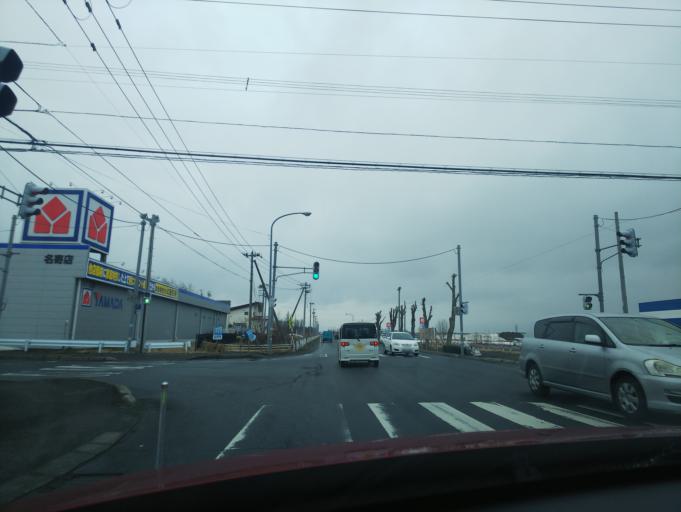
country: JP
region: Hokkaido
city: Nayoro
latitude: 44.3364
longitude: 142.4503
